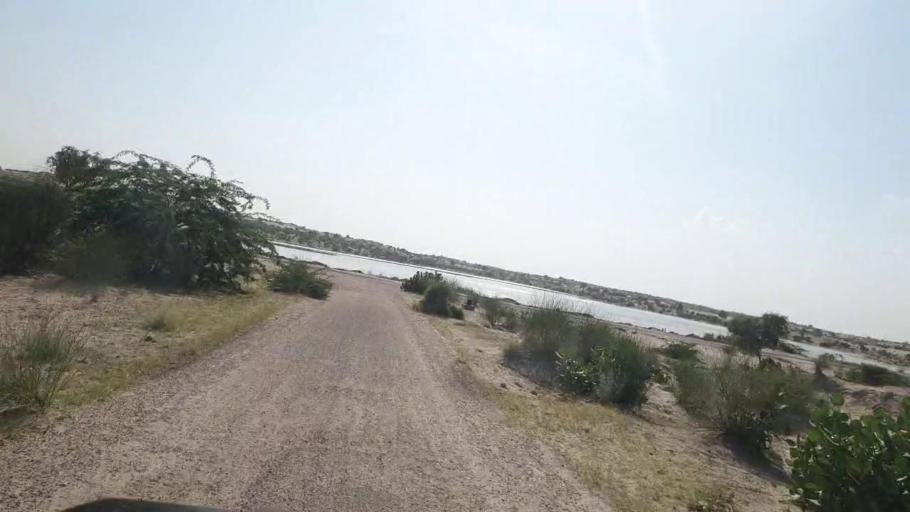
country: PK
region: Sindh
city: Chor
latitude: 25.5540
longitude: 70.2162
